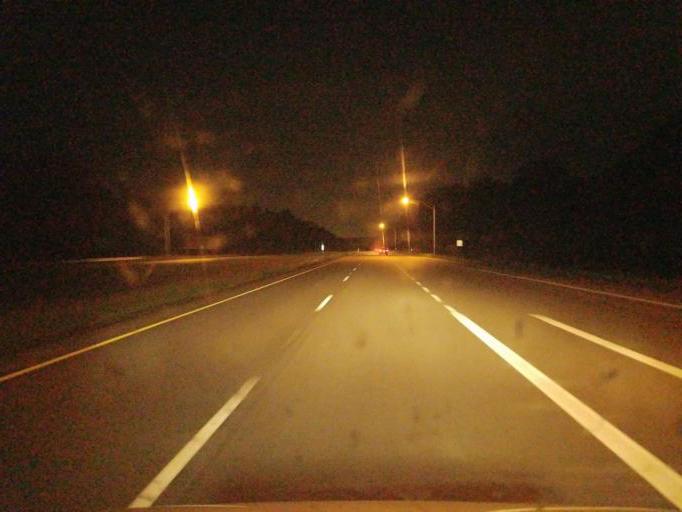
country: US
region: Ohio
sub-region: Geauga County
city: Bainbridge
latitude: 41.3883
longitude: -81.3433
